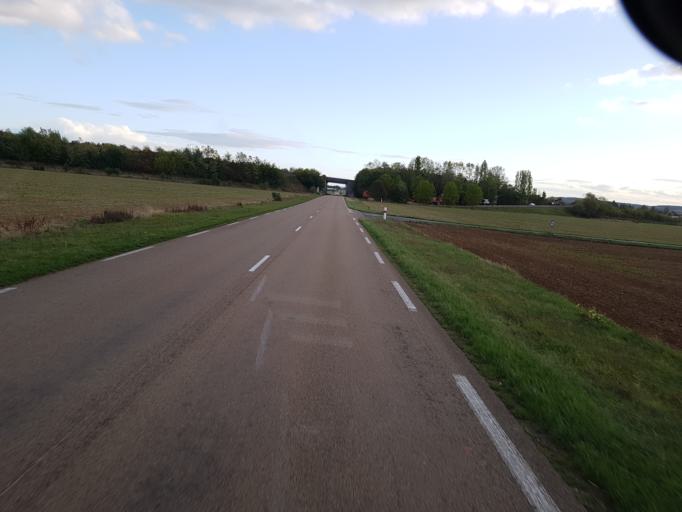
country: FR
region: Bourgogne
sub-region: Departement de l'Yonne
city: Soucy
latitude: 48.2596
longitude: 3.2832
